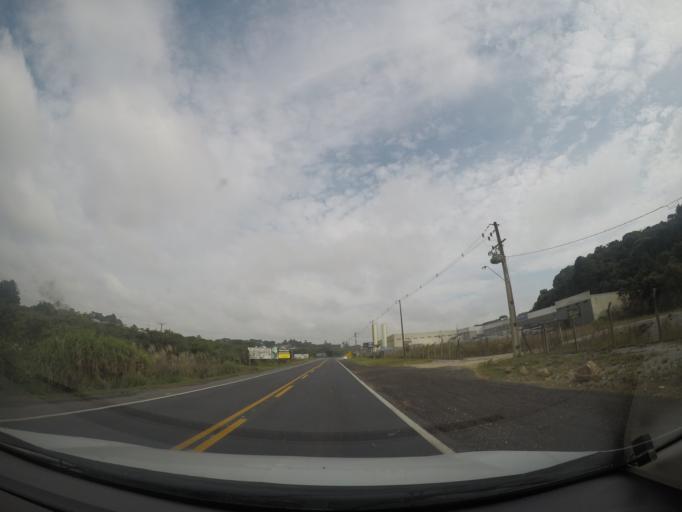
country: BR
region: Parana
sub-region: Colombo
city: Colombo
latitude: -25.3436
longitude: -49.2326
